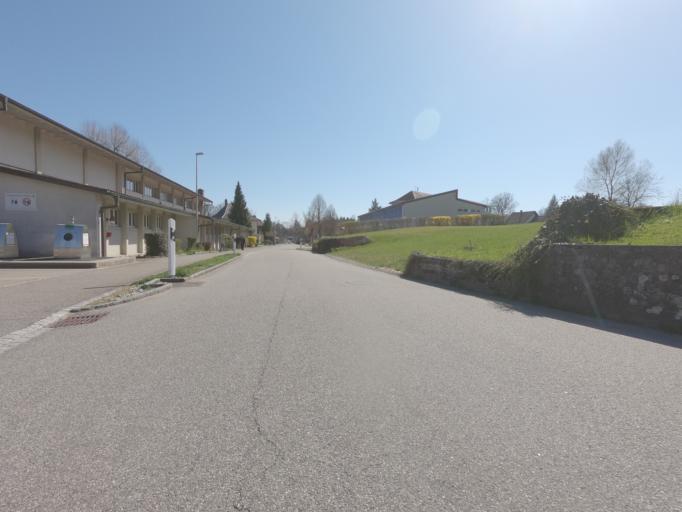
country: CH
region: Solothurn
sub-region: Bezirk Lebern
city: Riedholz
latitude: 47.2299
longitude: 7.5655
